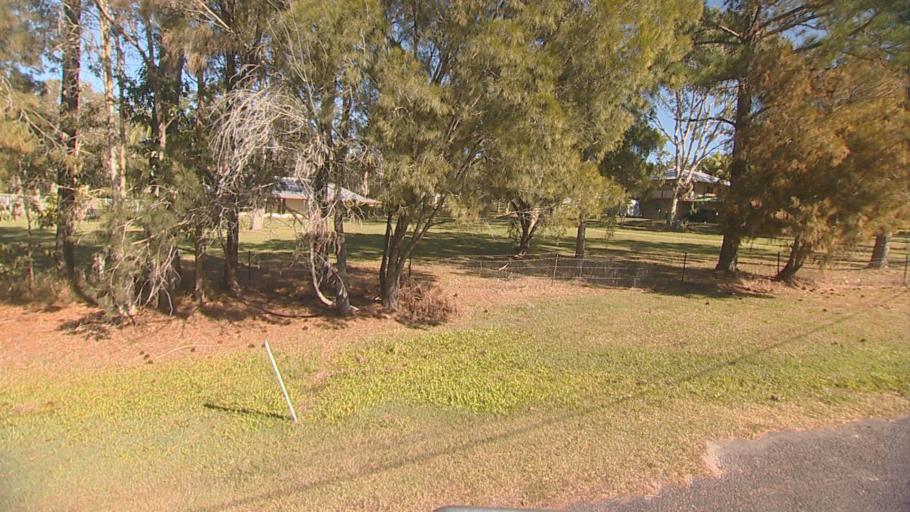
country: AU
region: Queensland
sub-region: Logan
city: Logan Reserve
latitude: -27.7029
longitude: 153.0796
